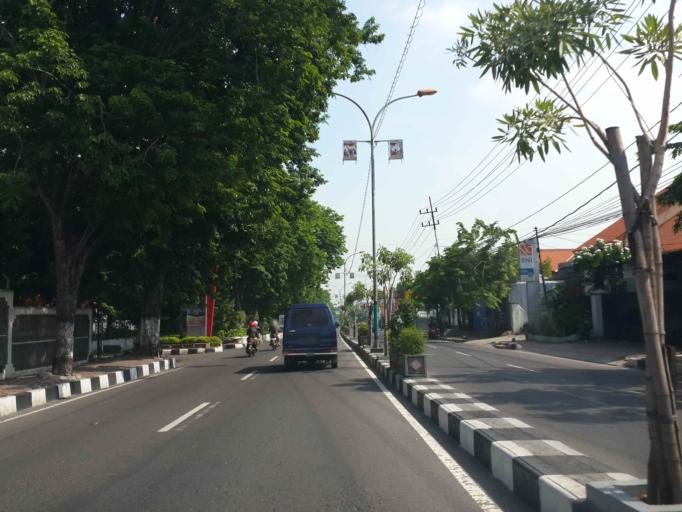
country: ID
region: East Java
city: Kebomas
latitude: -7.1805
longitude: 112.6497
